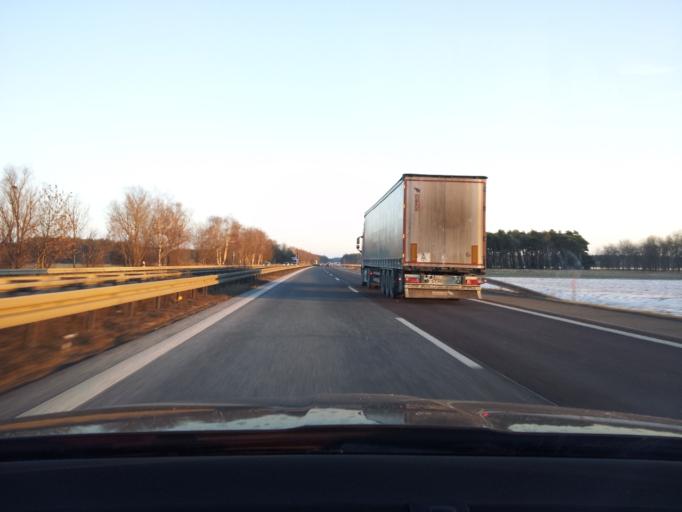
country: DE
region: Brandenburg
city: Kremmen
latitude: 52.7393
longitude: 12.9125
